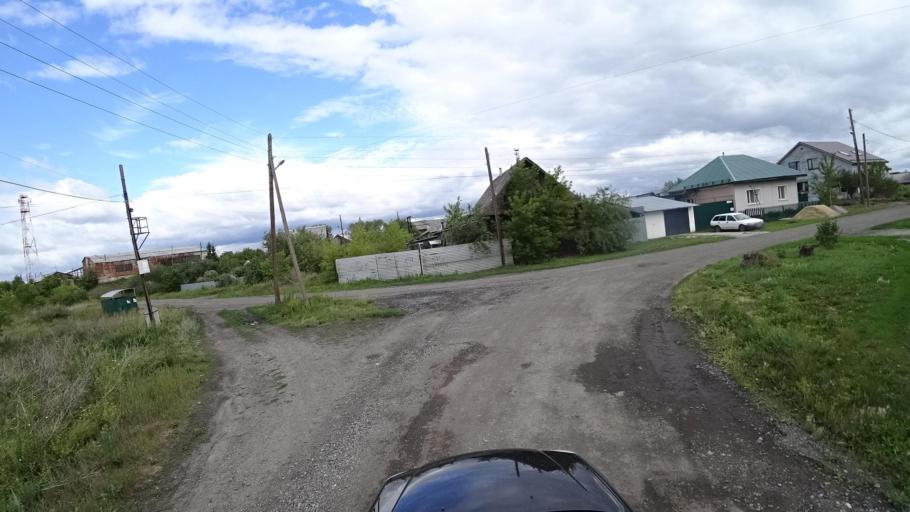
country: RU
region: Sverdlovsk
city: Kamyshlov
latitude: 56.8584
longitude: 62.7033
